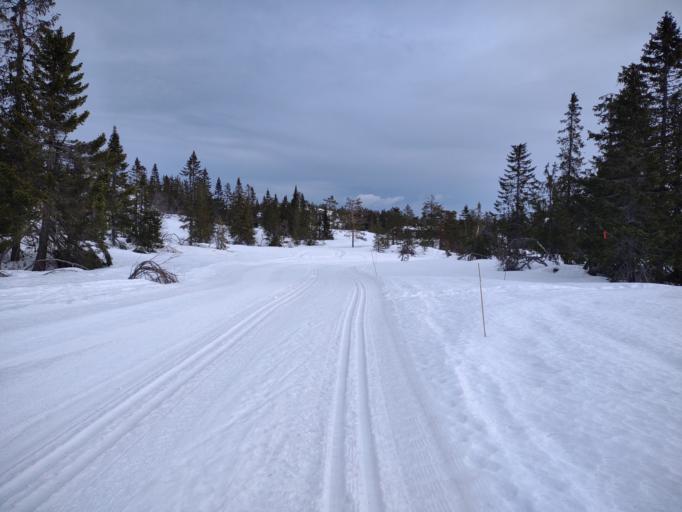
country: NO
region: Buskerud
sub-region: Flesberg
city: Lampeland
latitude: 59.7604
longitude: 9.4502
